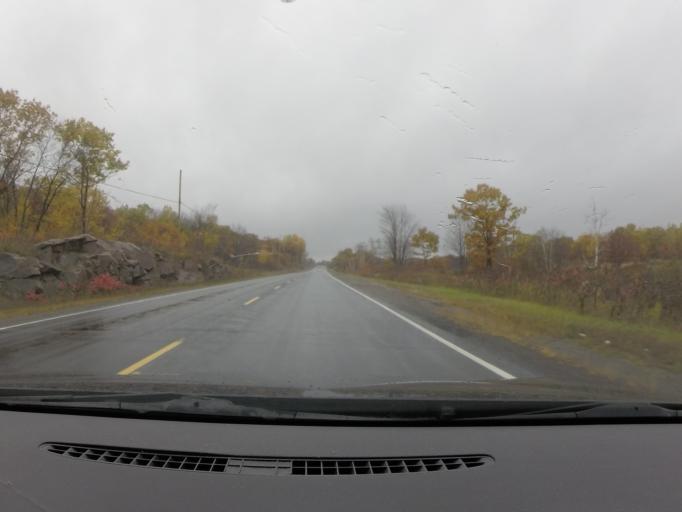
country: CA
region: Ontario
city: Greater Napanee
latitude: 44.6123
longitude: -77.1798
